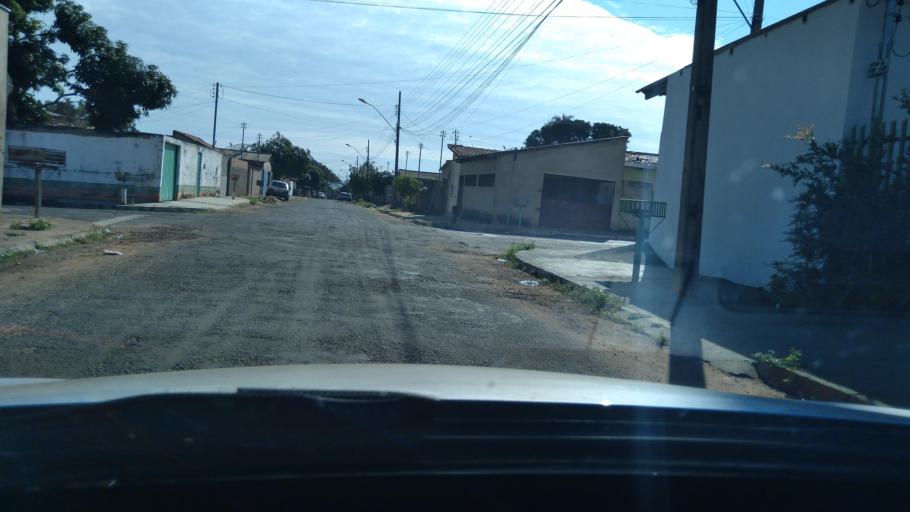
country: BR
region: Goias
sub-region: Mineiros
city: Mineiros
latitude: -17.5378
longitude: -52.5415
